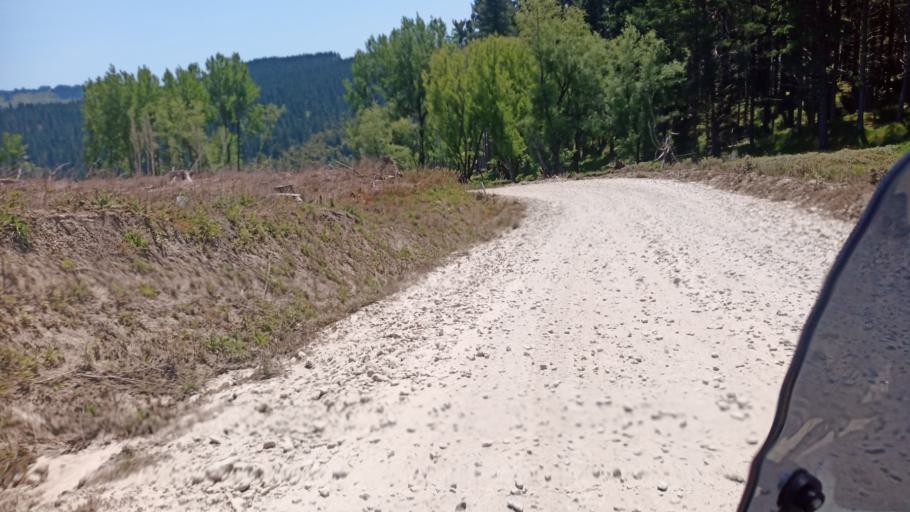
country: NZ
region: Gisborne
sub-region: Gisborne District
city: Gisborne
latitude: -38.2867
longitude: 178.0101
